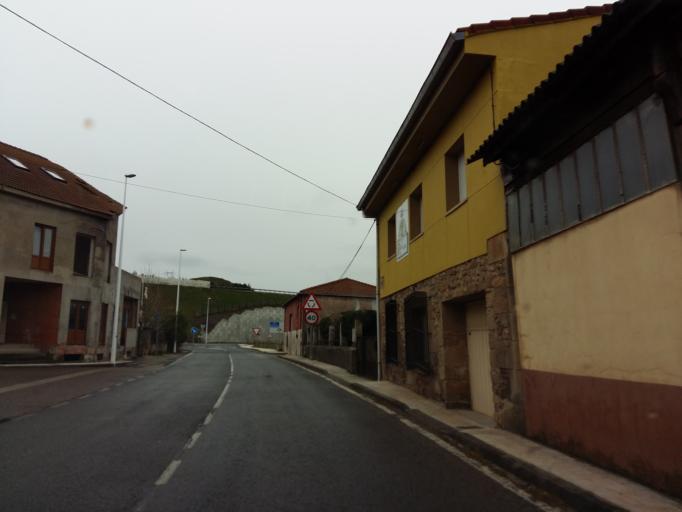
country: ES
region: Cantabria
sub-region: Provincia de Cantabria
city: Villaescusa
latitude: 42.9784
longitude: -4.1503
